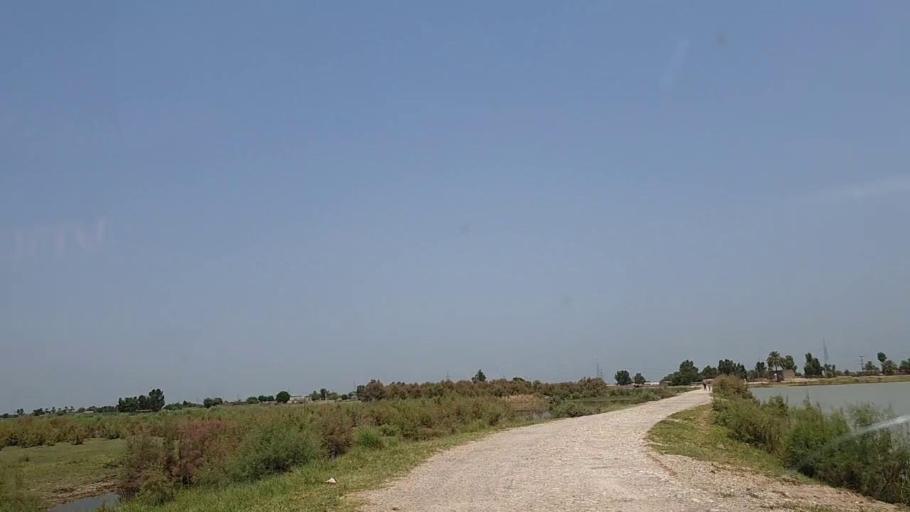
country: PK
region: Sindh
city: Ghotki
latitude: 27.9887
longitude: 69.3683
